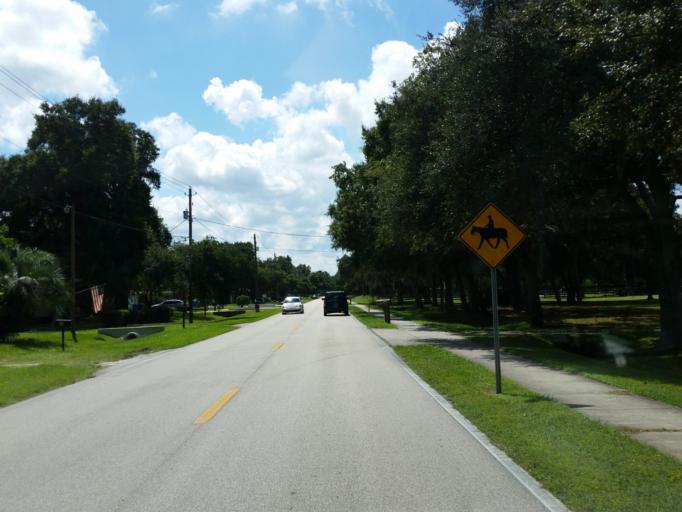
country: US
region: Florida
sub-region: Hillsborough County
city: Riverview
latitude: 27.8773
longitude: -82.3308
